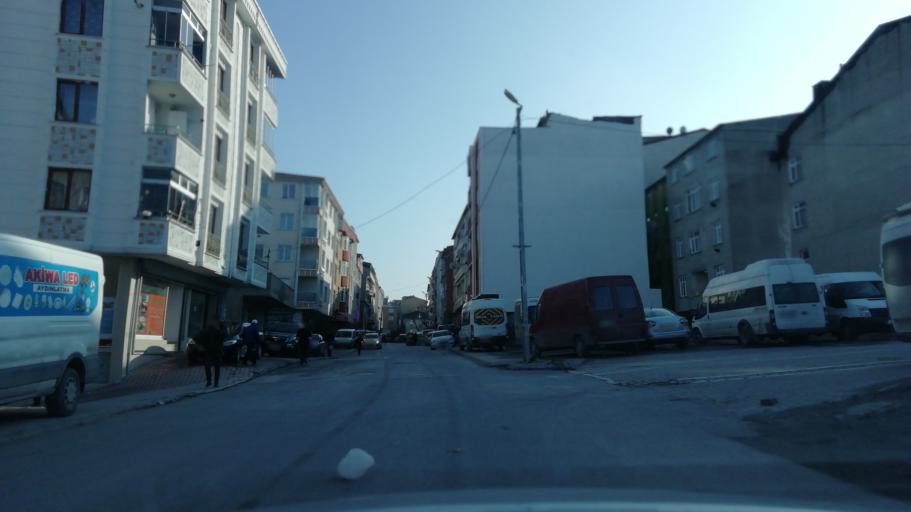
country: TR
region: Istanbul
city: Esenyurt
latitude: 41.0346
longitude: 28.6892
